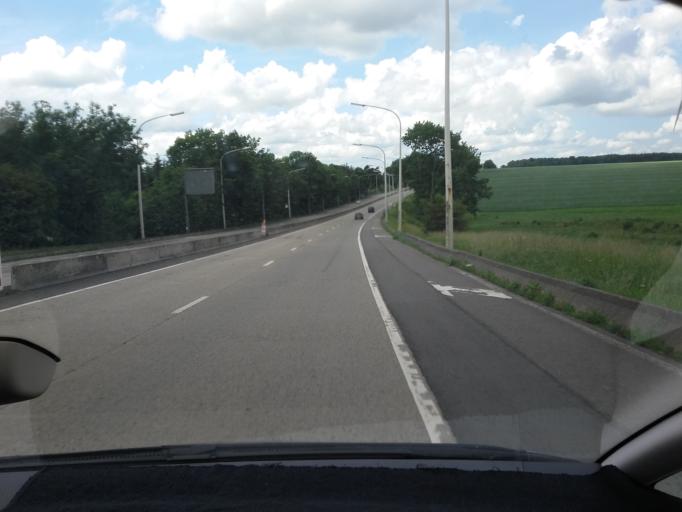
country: BE
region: Wallonia
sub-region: Province de Namur
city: Hamois
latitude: 50.2867
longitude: 5.1804
